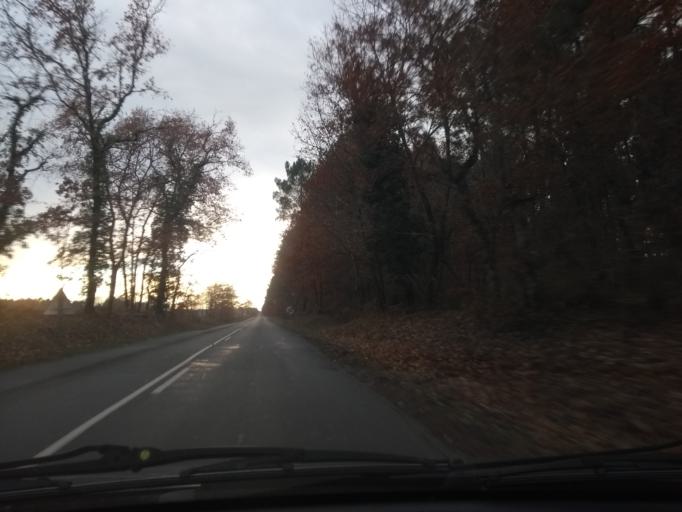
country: FR
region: Aquitaine
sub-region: Departement de la Gironde
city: Saucats
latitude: 44.6483
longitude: -0.6108
